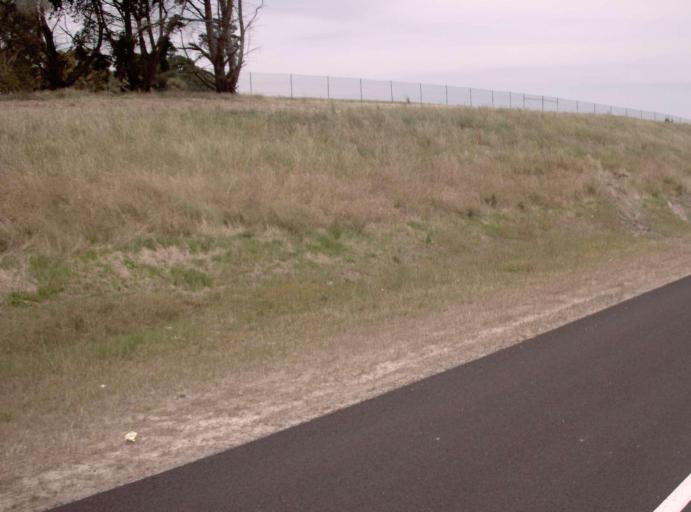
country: AU
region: Victoria
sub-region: Mornington Peninsula
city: Moorooduc
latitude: -38.2707
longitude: 145.0895
